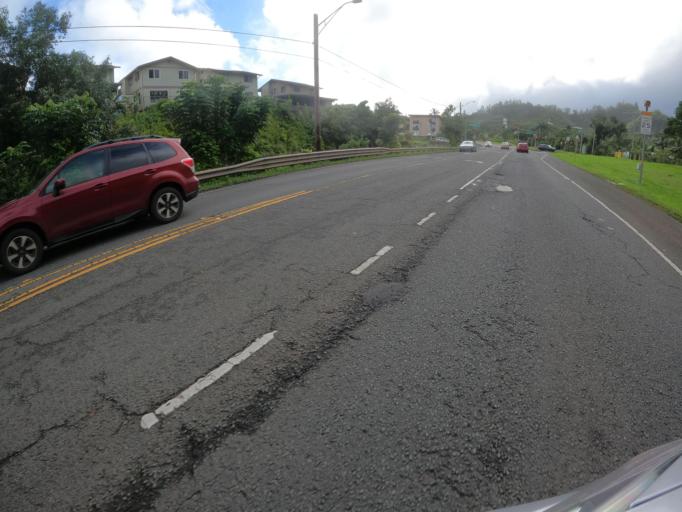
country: US
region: Hawaii
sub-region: Honolulu County
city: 'Ahuimanu
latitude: 21.4380
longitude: -157.8301
